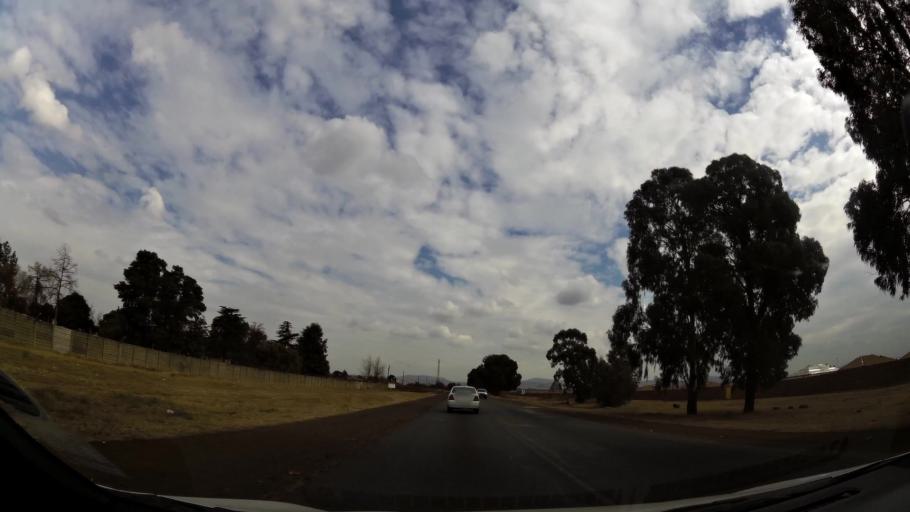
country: ZA
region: Gauteng
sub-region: Sedibeng District Municipality
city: Meyerton
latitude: -26.4193
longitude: 28.1152
